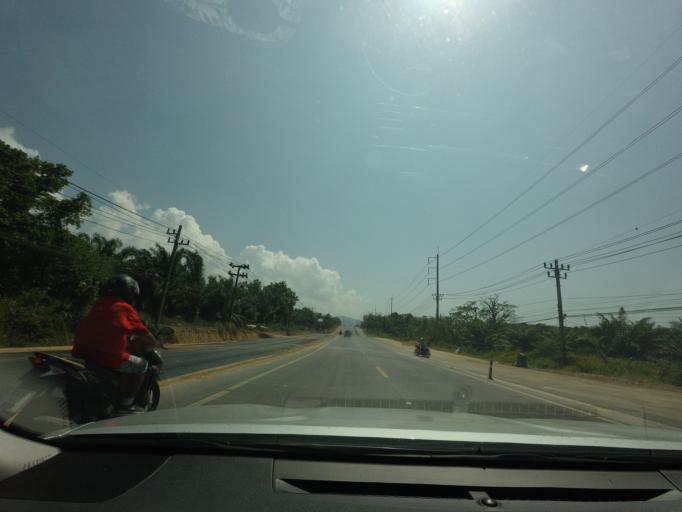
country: TH
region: Phangnga
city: Ban Khao Lak
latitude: 8.7197
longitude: 98.2565
